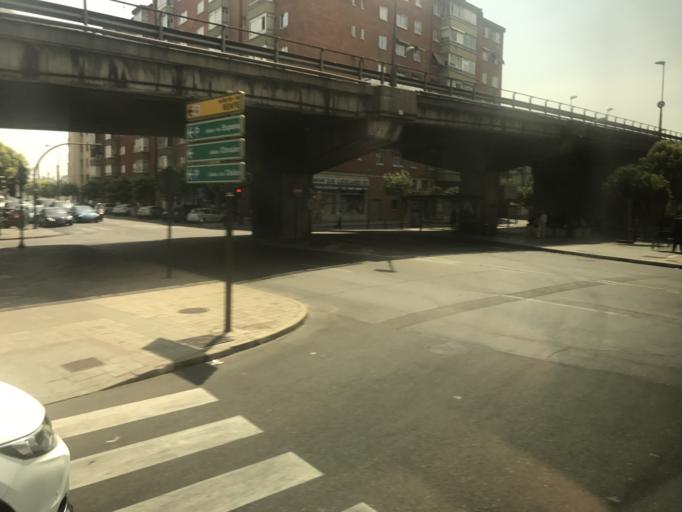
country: ES
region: Castille and Leon
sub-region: Provincia de Valladolid
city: Valladolid
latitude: 41.6413
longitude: -4.7315
